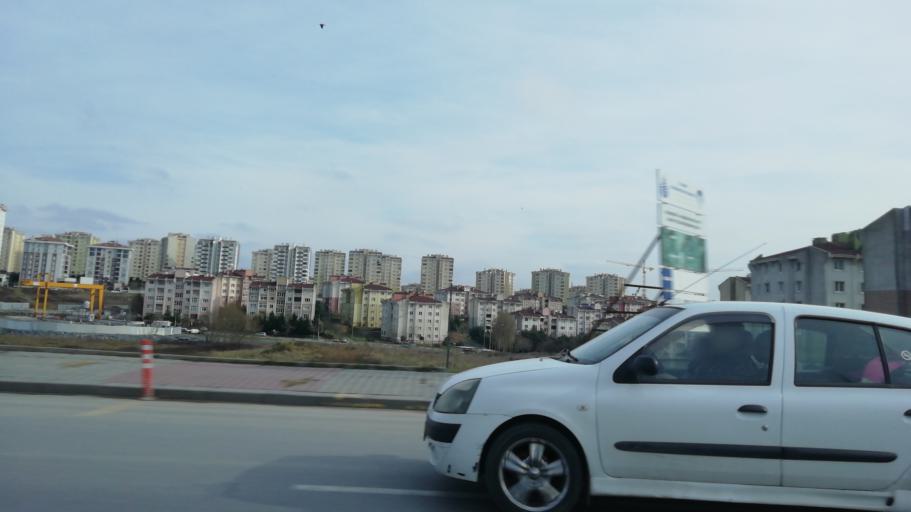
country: TR
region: Istanbul
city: Basaksehir
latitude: 41.1135
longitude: 28.7977
